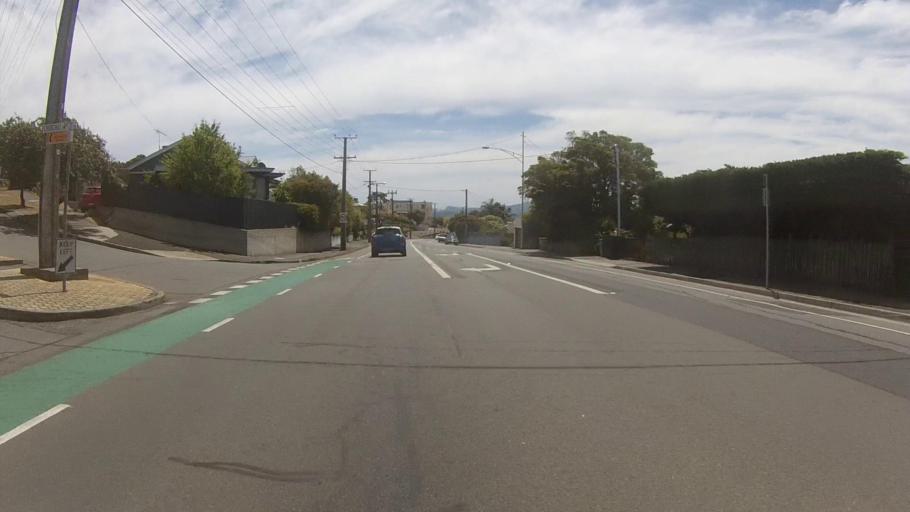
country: AU
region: Tasmania
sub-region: Kingborough
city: Taroona
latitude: -42.9175
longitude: 147.3591
